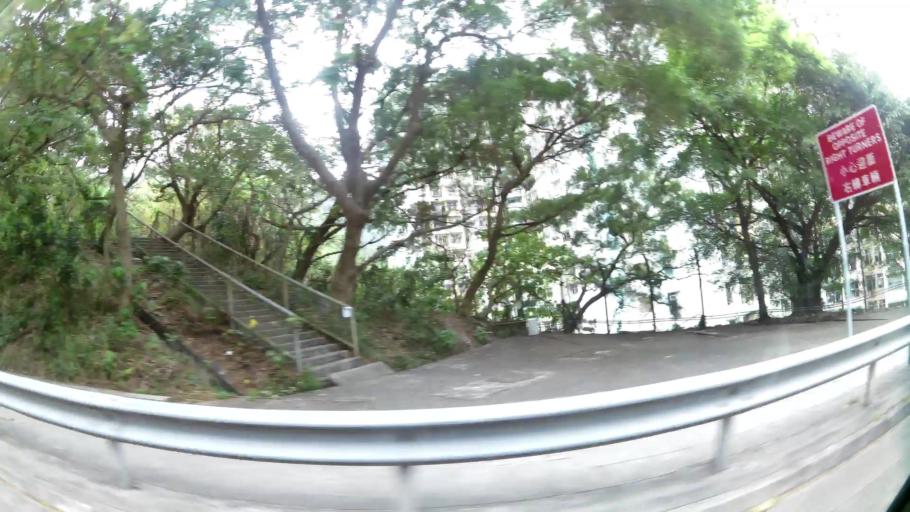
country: HK
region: Kowloon City
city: Kowloon
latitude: 22.2996
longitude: 114.2415
